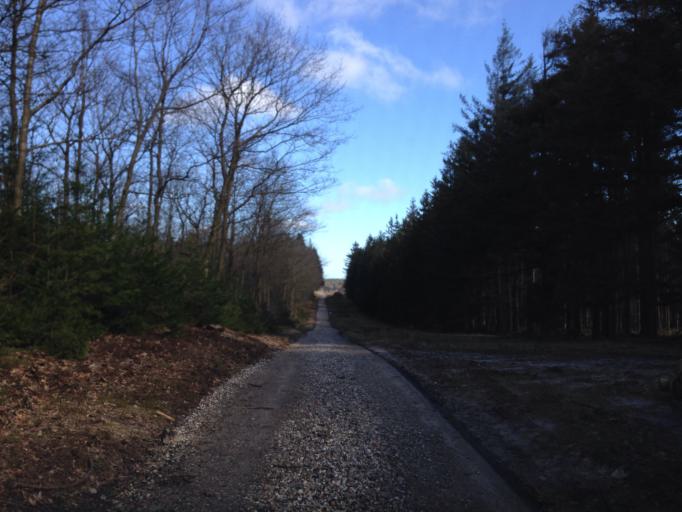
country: DK
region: Central Jutland
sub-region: Holstebro Kommune
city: Ulfborg
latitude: 56.2602
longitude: 8.4740
